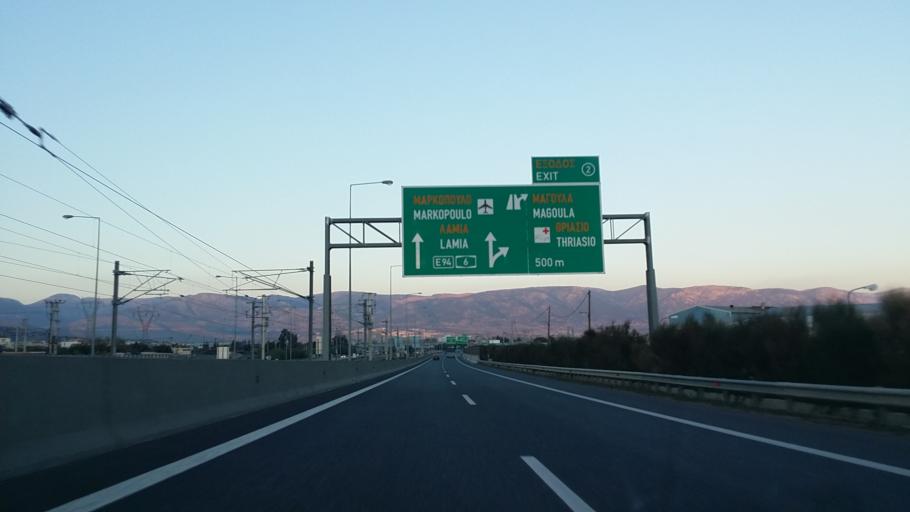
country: GR
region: Attica
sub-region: Nomarchia Dytikis Attikis
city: Magoula
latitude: 38.0673
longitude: 23.5238
